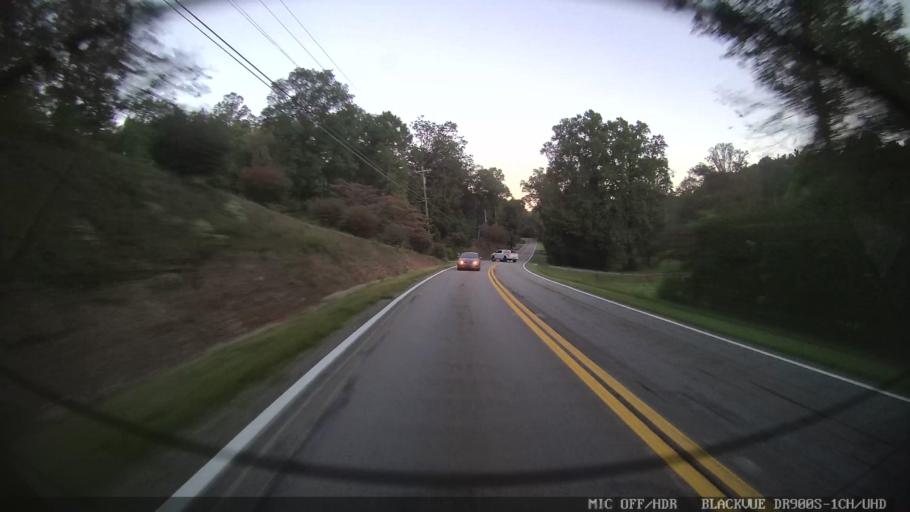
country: US
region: Georgia
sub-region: Gilmer County
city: Ellijay
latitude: 34.7129
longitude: -84.4994
